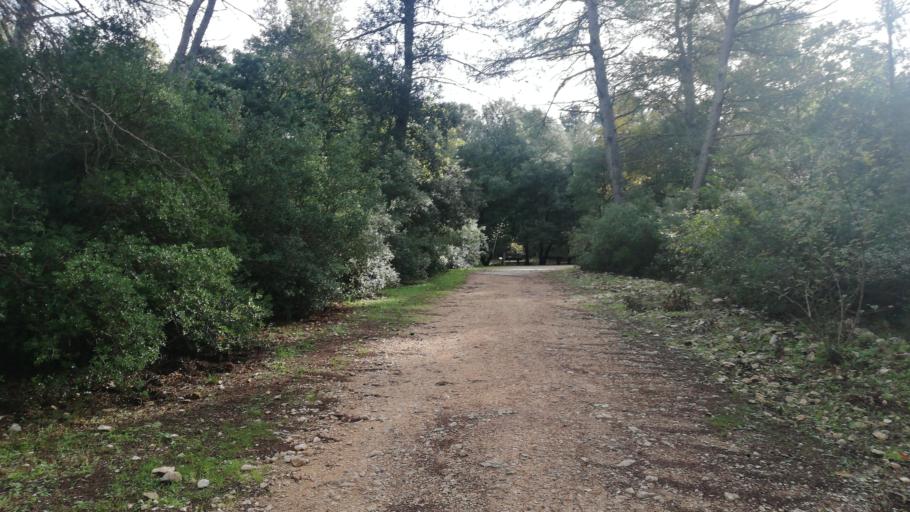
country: IT
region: Apulia
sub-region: Provincia di Bari
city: Cassano delle Murge
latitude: 40.8818
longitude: 16.7098
